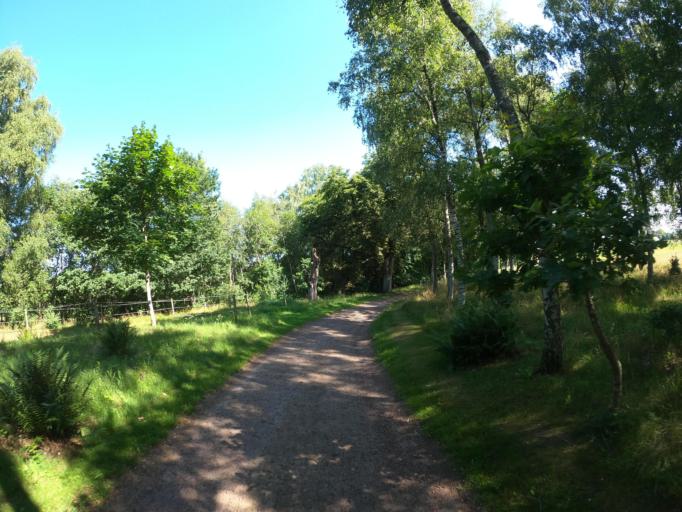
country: SE
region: Skane
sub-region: Lunds Kommun
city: Veberod
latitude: 55.6741
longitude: 13.4153
